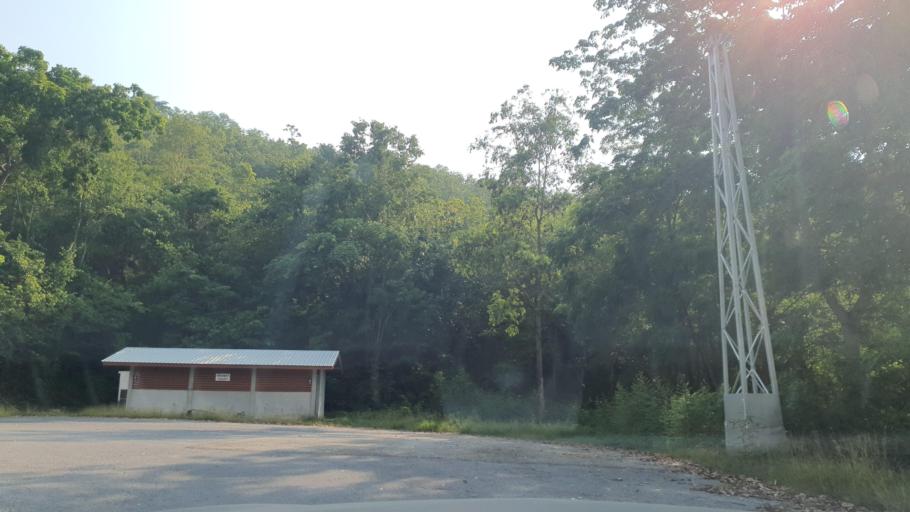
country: TH
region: Kanchanaburi
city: Sai Yok
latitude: 14.2312
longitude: 99.2288
